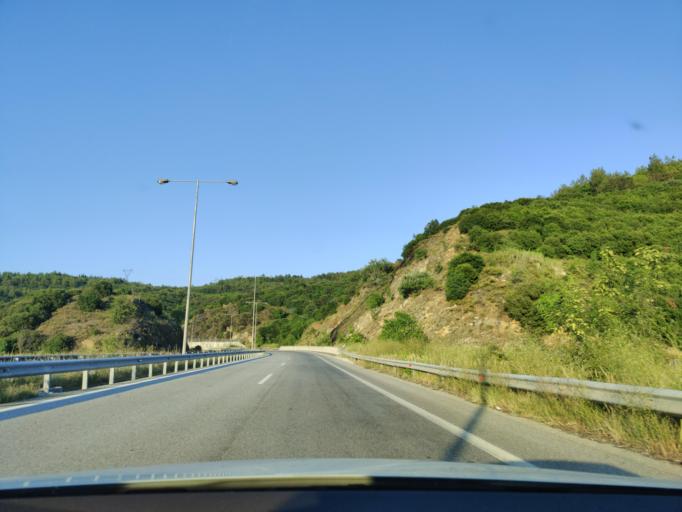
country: GR
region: East Macedonia and Thrace
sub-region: Nomos Kavalas
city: Kavala
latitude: 40.9554
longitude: 24.3892
